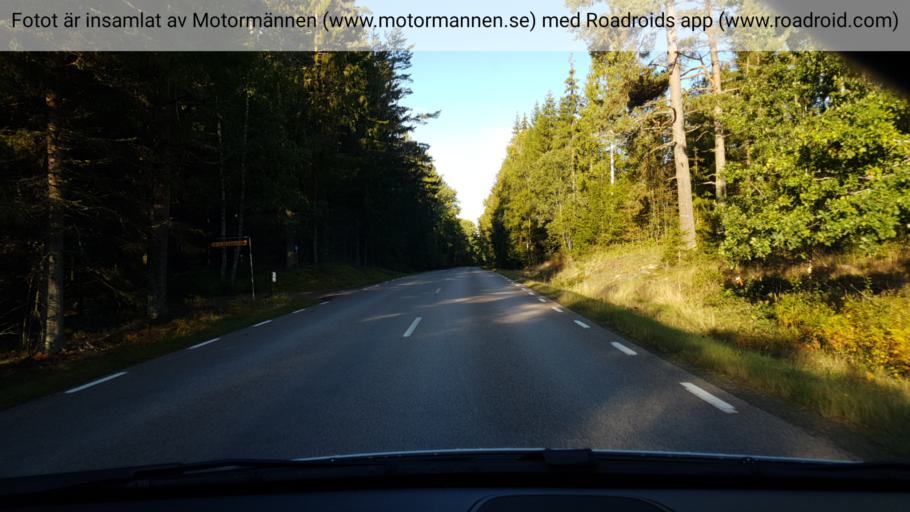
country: SE
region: Vaestra Goetaland
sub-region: Gotene Kommun
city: Goetene
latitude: 58.5447
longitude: 13.6575
